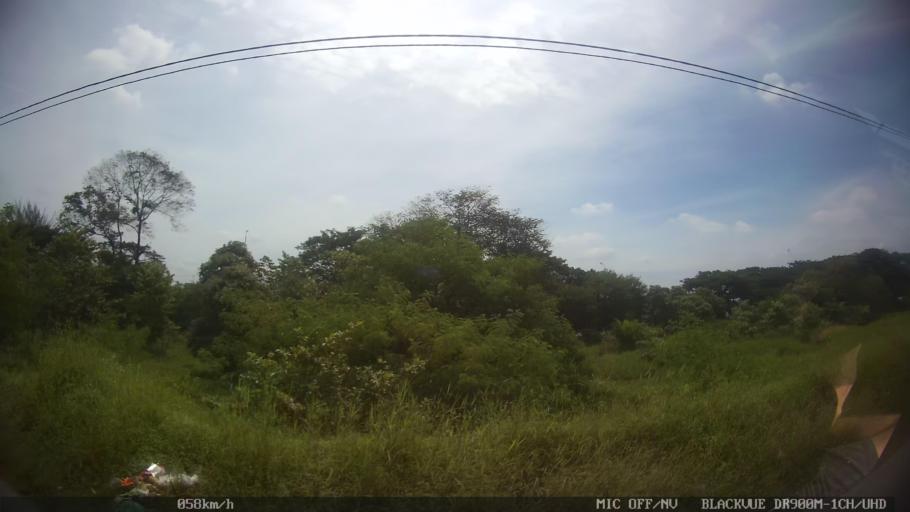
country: ID
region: North Sumatra
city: Medan
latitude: 3.6381
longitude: 98.7084
